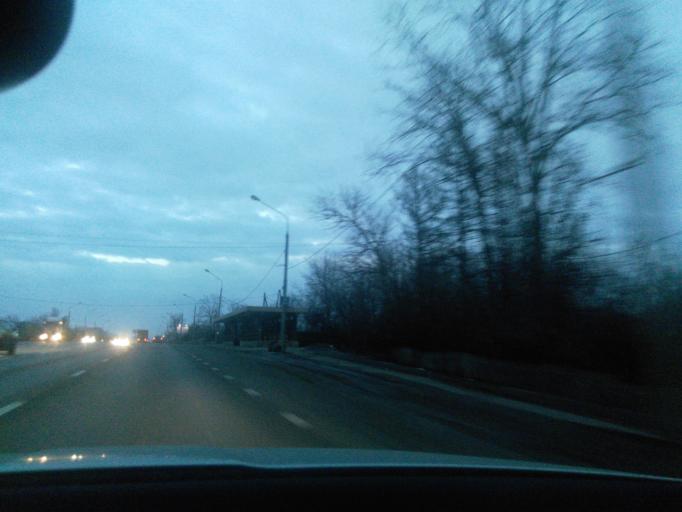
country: RU
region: Moskovskaya
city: Novopodrezkovo
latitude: 55.9263
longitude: 37.3845
